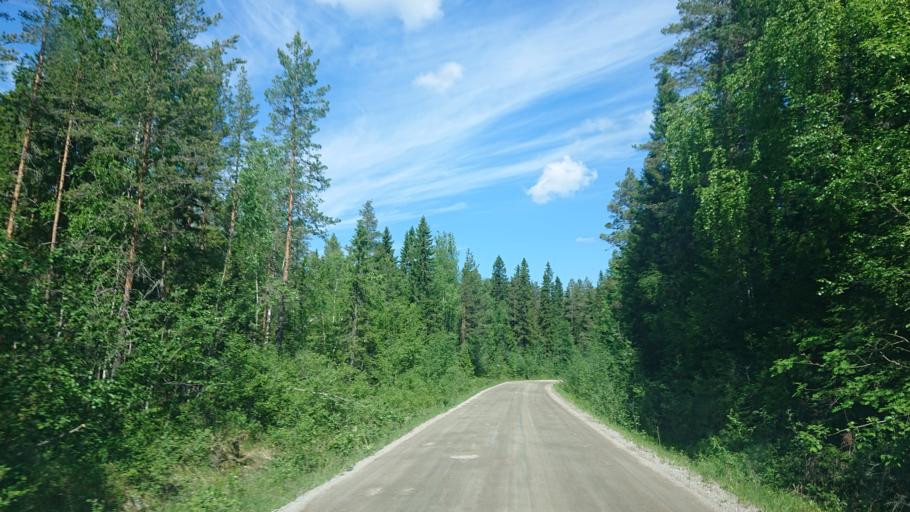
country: SE
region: Vaesternorrland
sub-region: Solleftea Kommun
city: Solleftea
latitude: 62.9583
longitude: 17.1467
